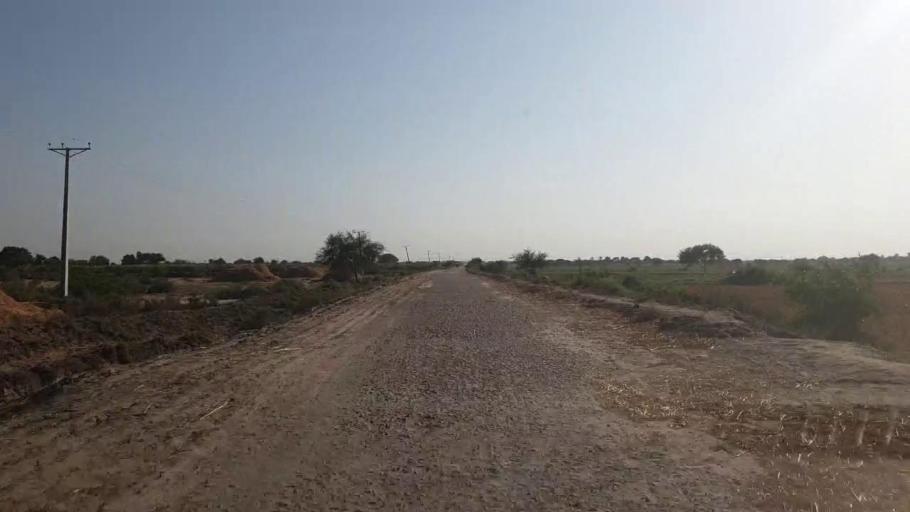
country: PK
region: Sindh
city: Talhar
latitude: 24.9401
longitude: 68.7517
